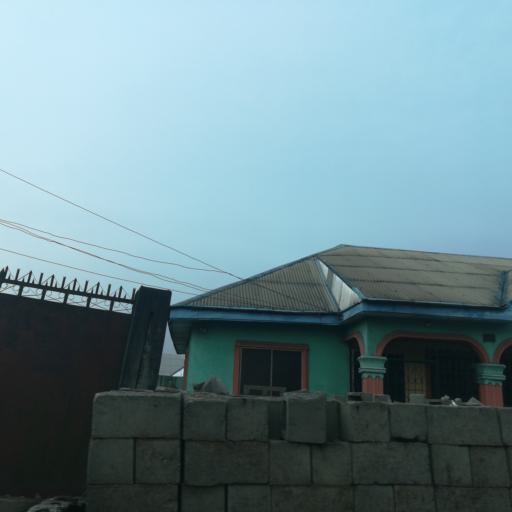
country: NG
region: Rivers
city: Port Harcourt
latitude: 4.7491
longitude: 7.0083
